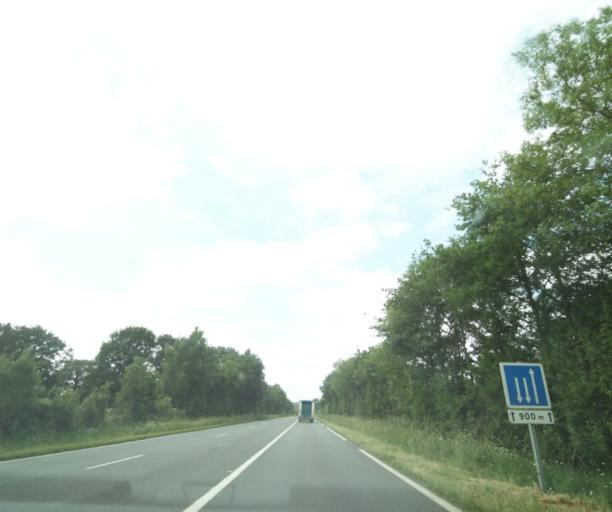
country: FR
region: Poitou-Charentes
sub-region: Departement des Deux-Sevres
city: Champdeniers-Saint-Denis
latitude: 46.4920
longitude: -0.3480
